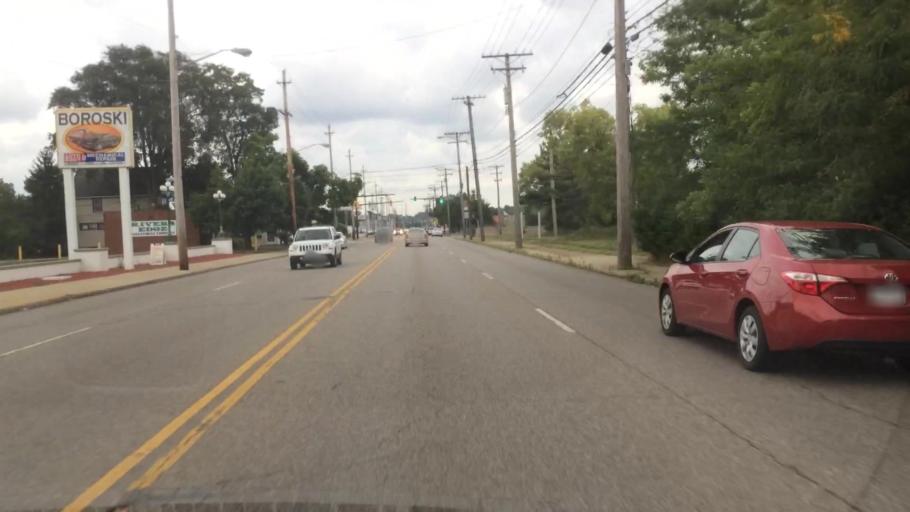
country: US
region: Ohio
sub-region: Cuyahoga County
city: Maple Heights
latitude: 41.4071
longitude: -81.5587
